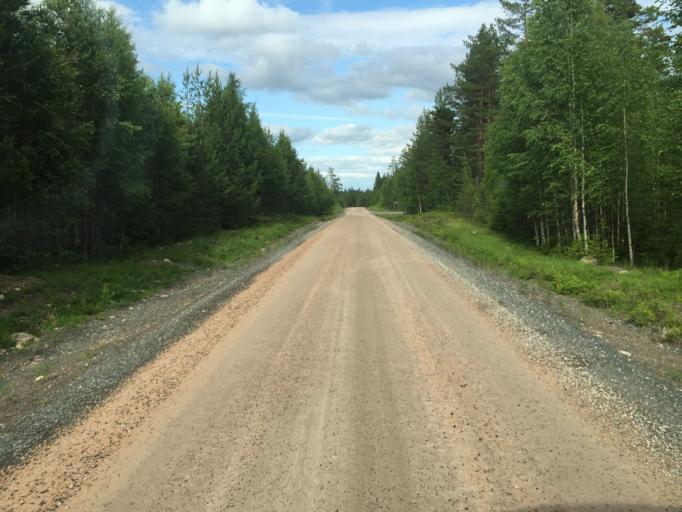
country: SE
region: Dalarna
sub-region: Malung-Saelens kommun
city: Malung
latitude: 60.9188
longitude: 13.7839
